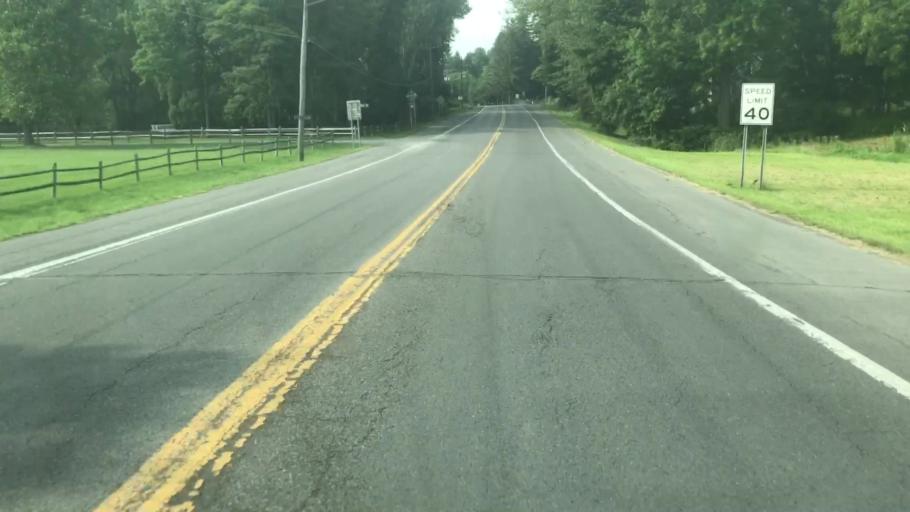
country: US
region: New York
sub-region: Cayuga County
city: Melrose Park
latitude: 42.9040
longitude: -76.5451
